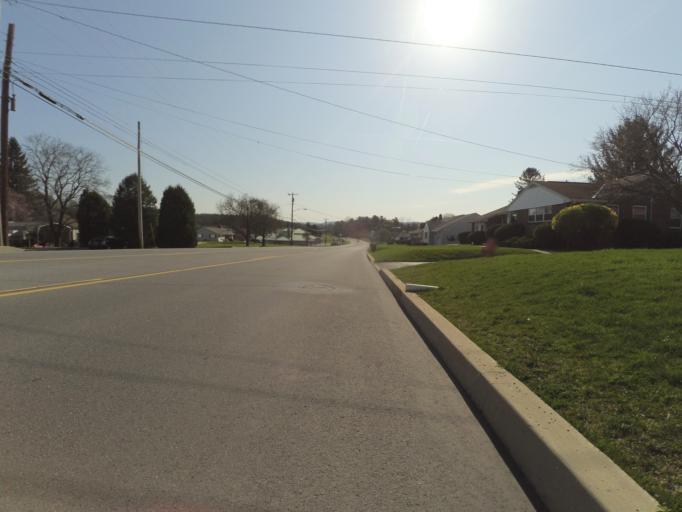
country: US
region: Pennsylvania
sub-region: Centre County
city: Bellefonte
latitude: 40.9147
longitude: -77.7525
